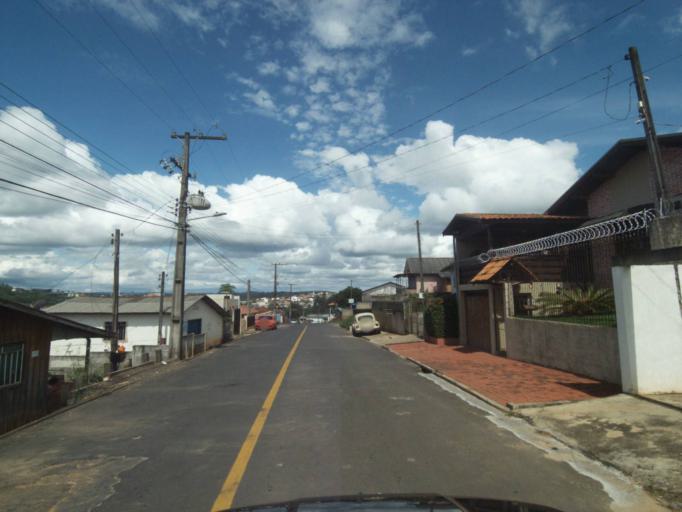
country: BR
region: Parana
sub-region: Telemaco Borba
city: Telemaco Borba
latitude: -24.3152
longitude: -50.6274
